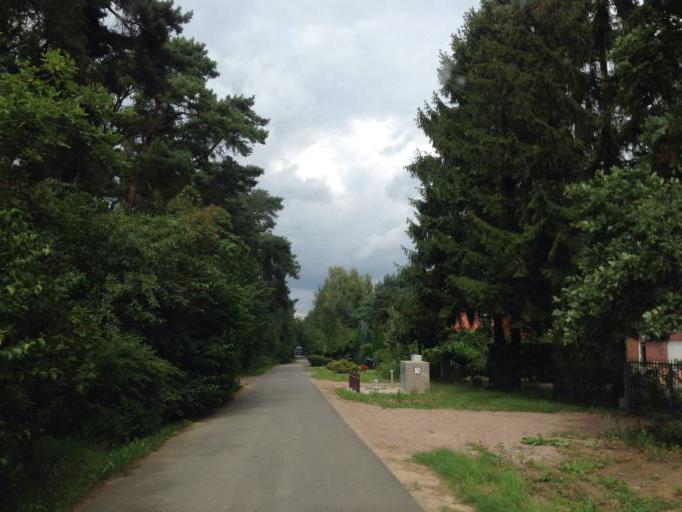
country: DE
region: Lower Saxony
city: Adendorf
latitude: 53.2946
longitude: 10.4406
